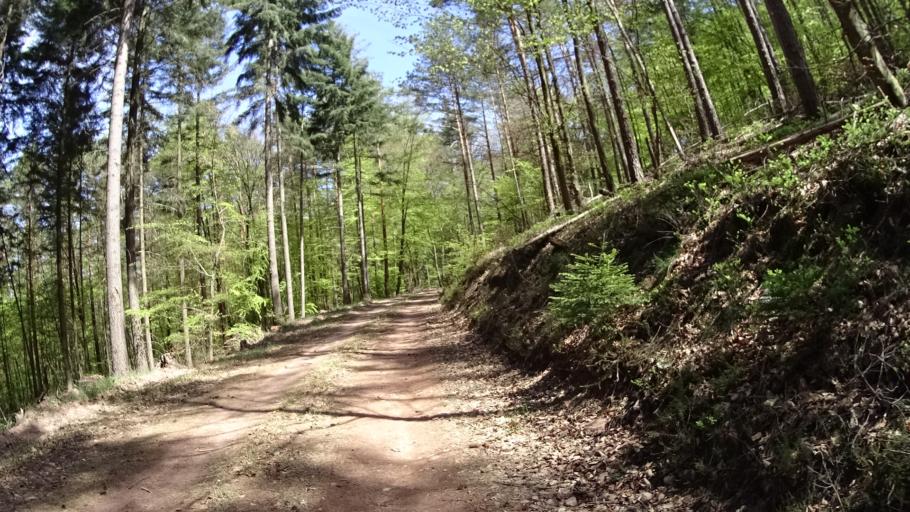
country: DE
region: Rheinland-Pfalz
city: Ramberg
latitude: 49.2979
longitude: 8.0018
